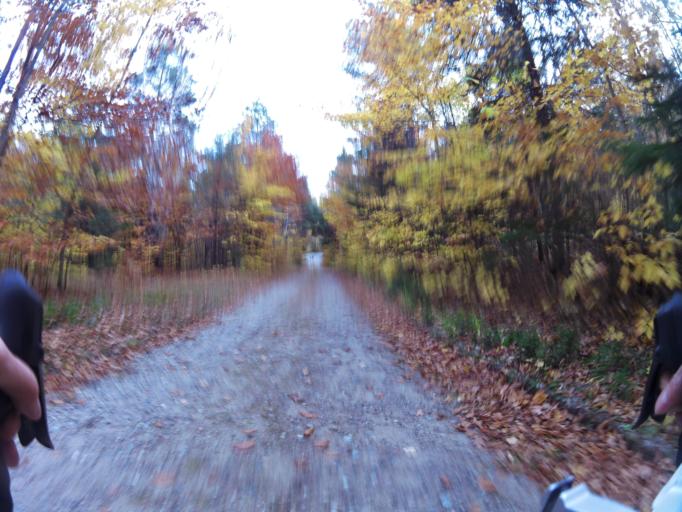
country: CA
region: Quebec
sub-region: Outaouais
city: Wakefield
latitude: 45.6115
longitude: -76.0126
